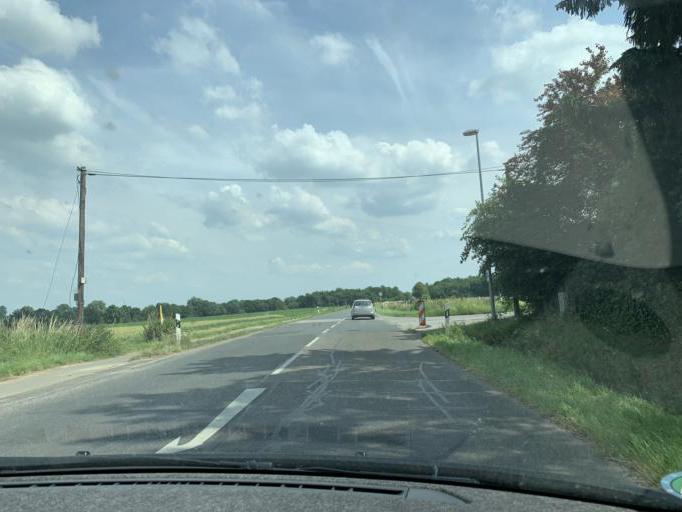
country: DE
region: North Rhine-Westphalia
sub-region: Regierungsbezirk Koln
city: Bedburg
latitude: 50.9799
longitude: 6.5798
